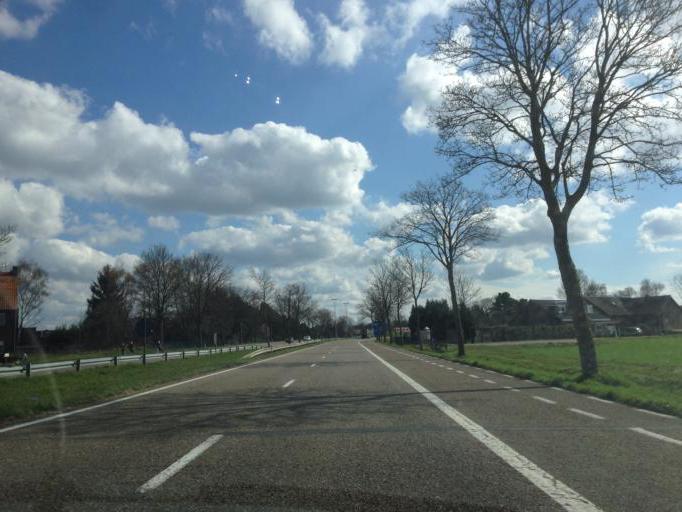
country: BE
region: Flanders
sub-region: Provincie Limburg
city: Bree
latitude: 51.1432
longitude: 5.5867
